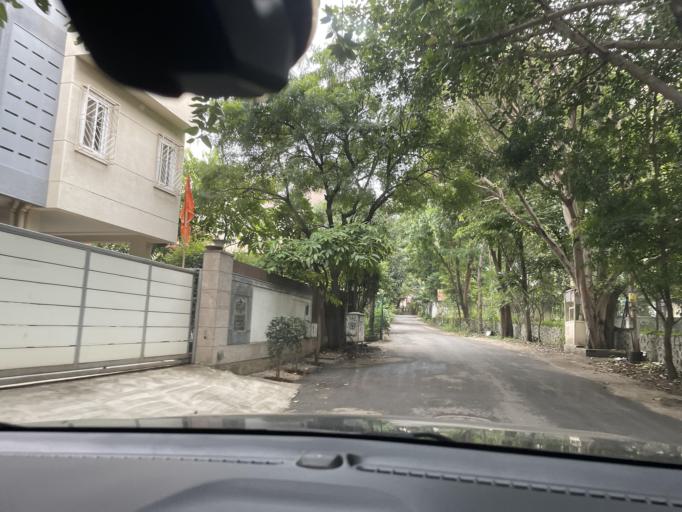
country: IN
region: Maharashtra
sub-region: Pune Division
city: Kharakvasla
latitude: 18.5133
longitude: 73.7796
